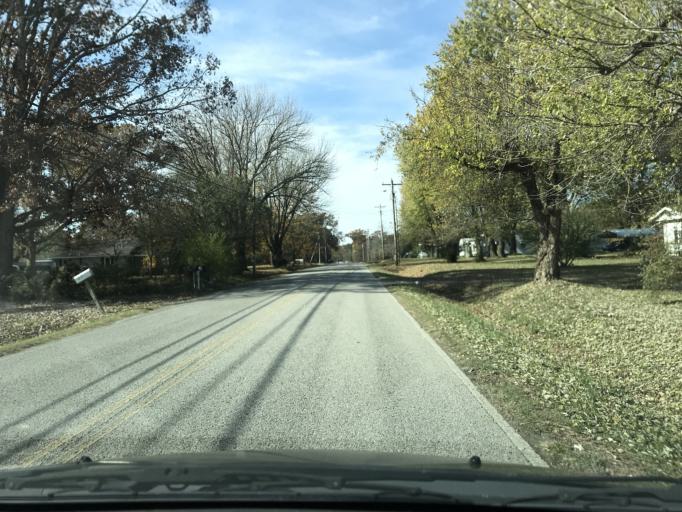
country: US
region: Tennessee
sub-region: Coffee County
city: Tullahoma
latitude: 35.3899
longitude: -86.1602
